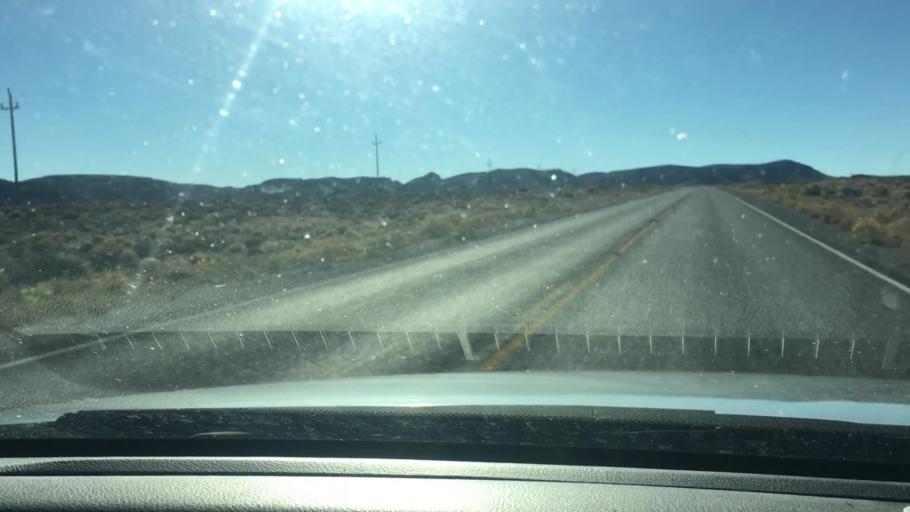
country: US
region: Nevada
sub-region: Nye County
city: Tonopah
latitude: 38.1240
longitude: -116.8654
